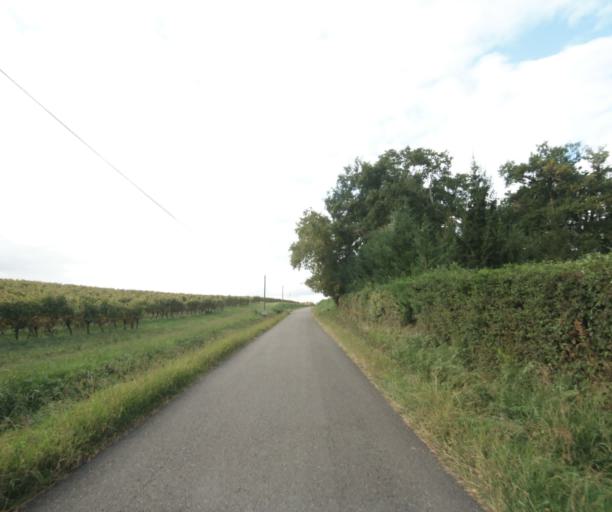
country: FR
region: Midi-Pyrenees
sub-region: Departement du Gers
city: Eauze
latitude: 43.8793
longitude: 0.0807
